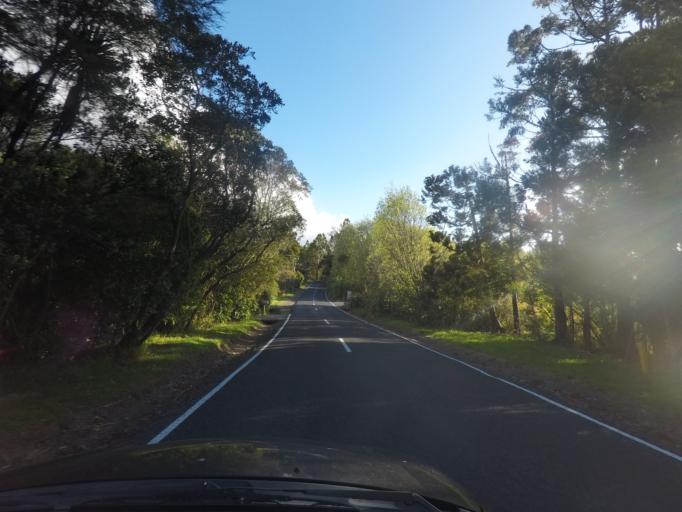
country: NZ
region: Auckland
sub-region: Auckland
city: Titirangi
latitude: -36.9291
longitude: 174.6192
